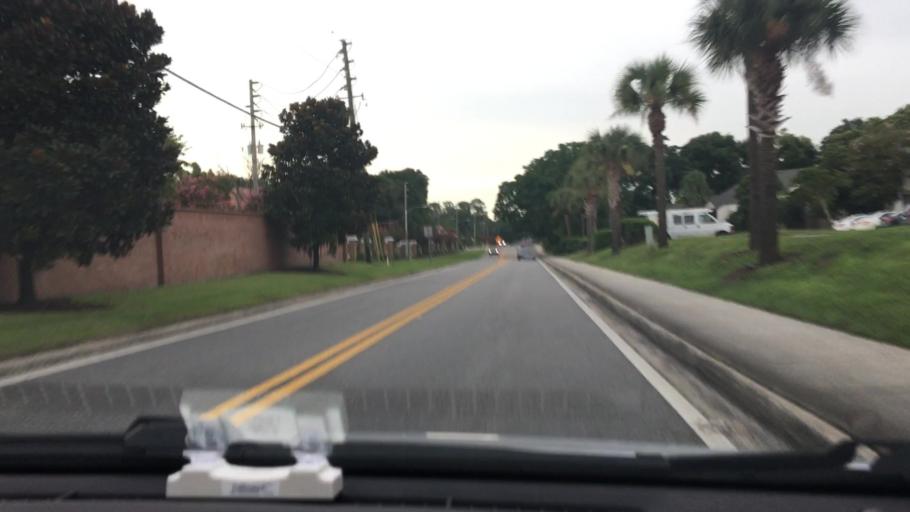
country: US
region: Florida
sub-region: Seminole County
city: Altamonte Springs
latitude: 28.6484
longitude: -81.3903
